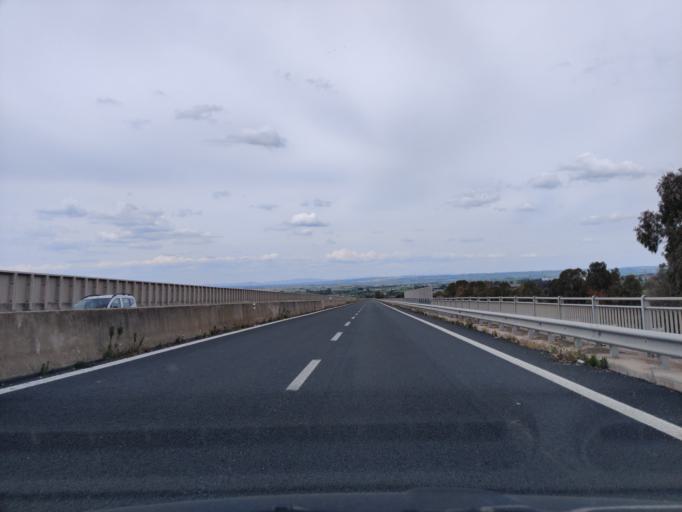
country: IT
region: Latium
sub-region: Citta metropolitana di Roma Capitale
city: Aurelia
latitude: 42.1395
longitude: 11.7942
